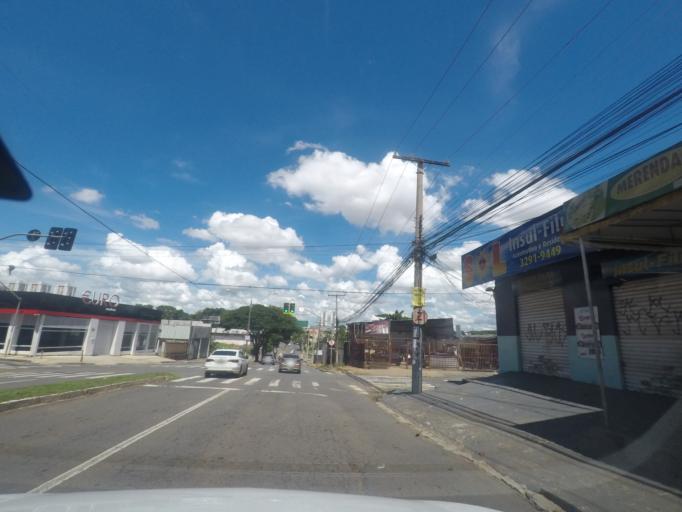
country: BR
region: Goias
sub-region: Goiania
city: Goiania
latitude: -16.6847
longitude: -49.2907
